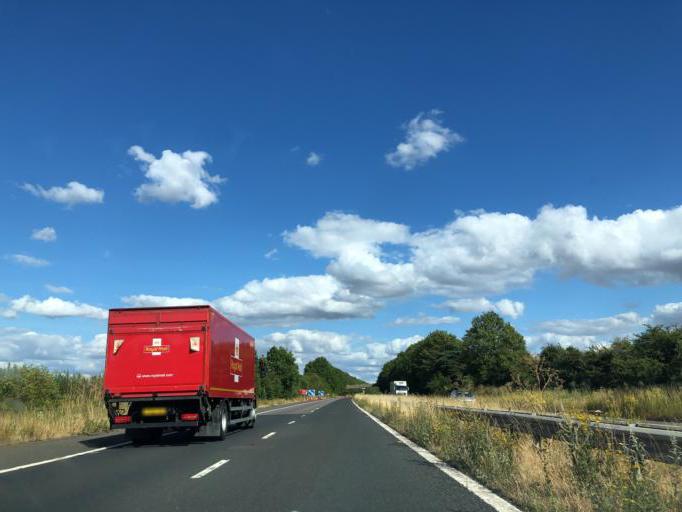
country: GB
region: England
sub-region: Warwickshire
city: Rugby
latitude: 52.3369
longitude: -1.2043
